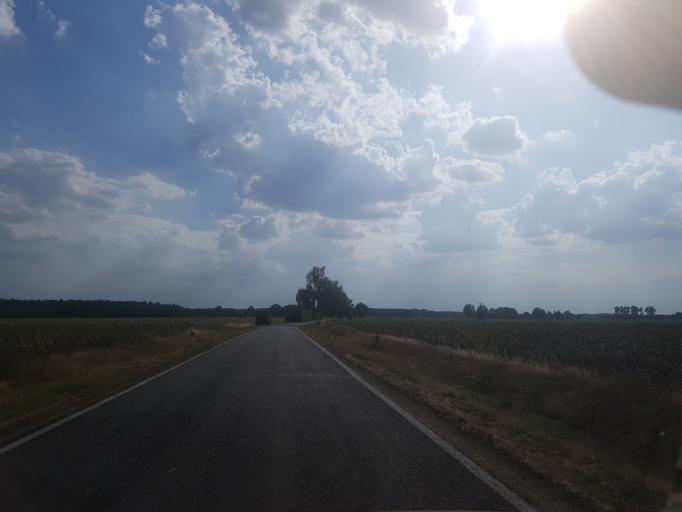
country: DE
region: Saxony-Anhalt
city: Holzdorf
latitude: 51.8013
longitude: 13.2226
